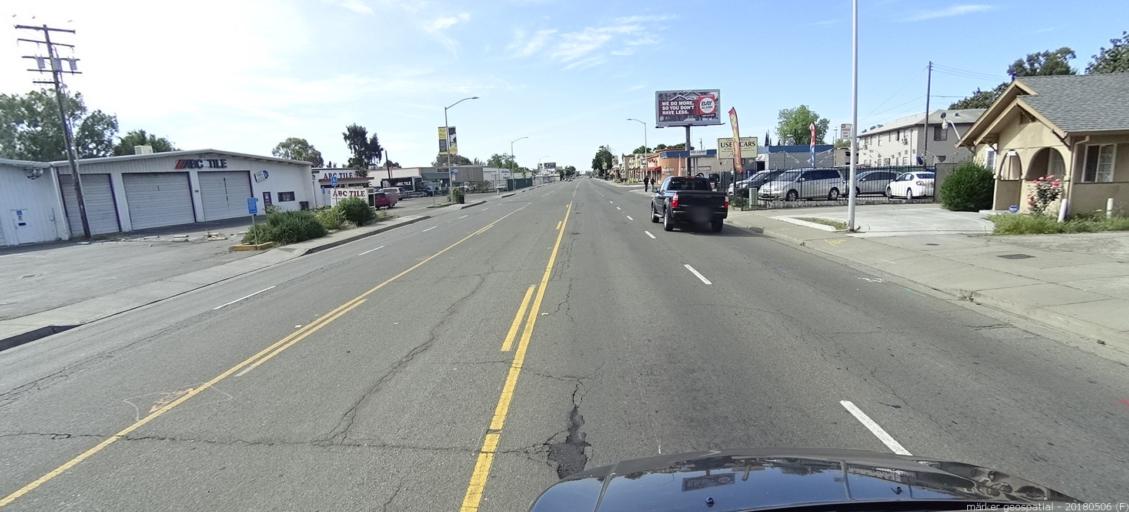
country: US
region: California
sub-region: Sacramento County
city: Parkway
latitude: 38.5384
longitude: -121.4752
